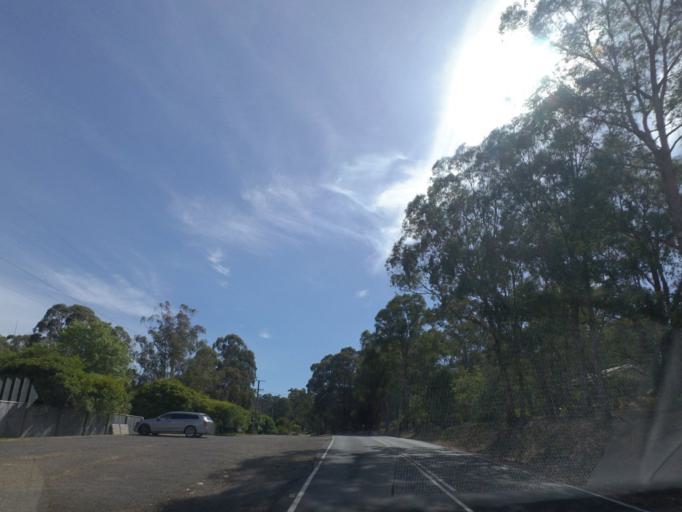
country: AU
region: Victoria
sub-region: Nillumbik
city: Saint Andrews
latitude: -37.5972
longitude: 145.2788
